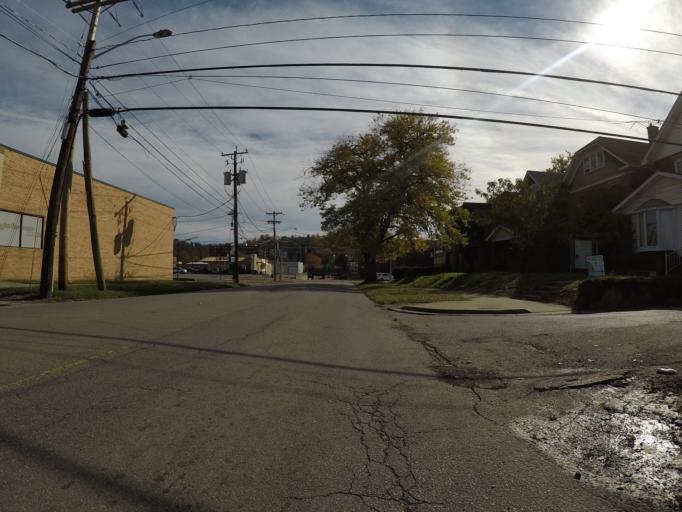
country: US
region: West Virginia
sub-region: Cabell County
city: Huntington
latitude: 38.4150
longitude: -82.4567
